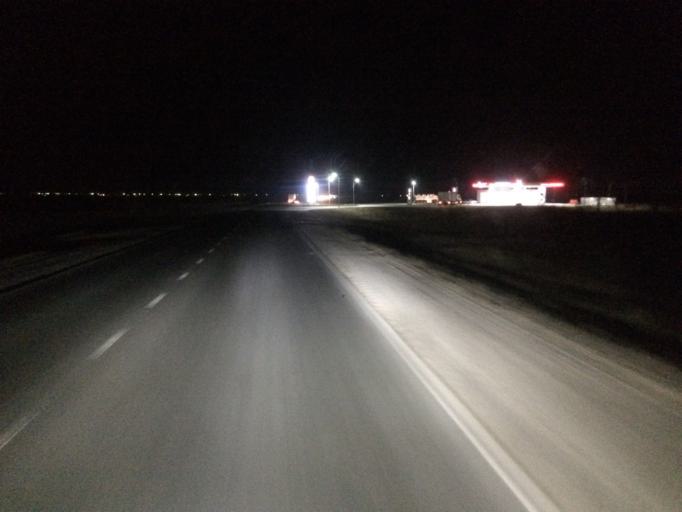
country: KZ
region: Batys Qazaqstan
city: Oral
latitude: 51.2173
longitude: 51.2773
